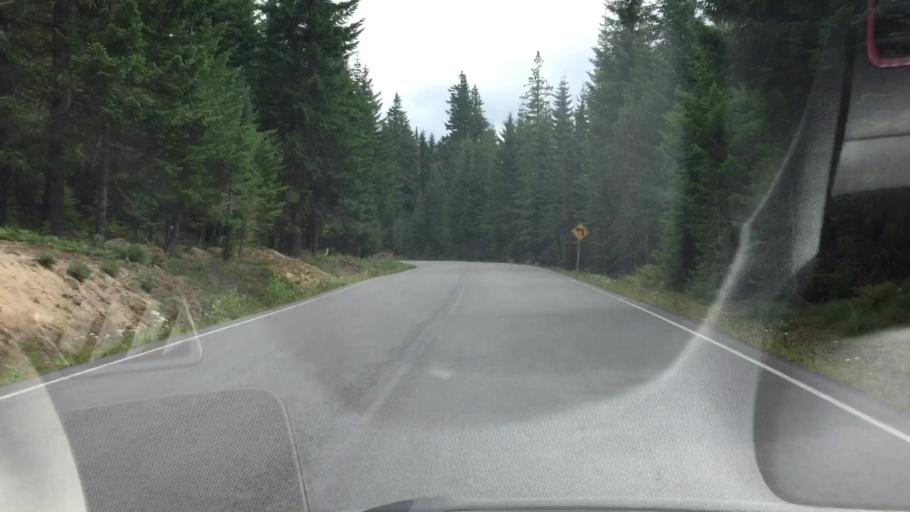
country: US
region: Washington
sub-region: Klickitat County
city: White Salmon
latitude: 46.1905
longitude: -121.6494
